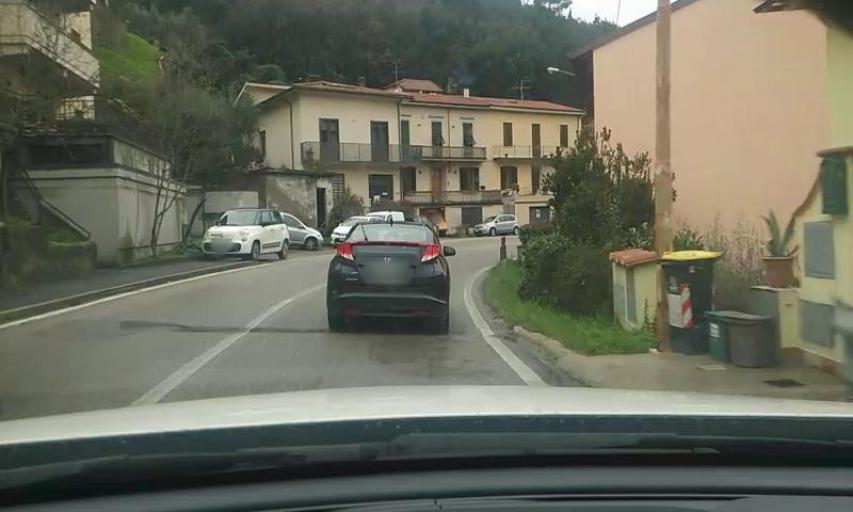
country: IT
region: Tuscany
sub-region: Provincia di Prato
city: Vaiano
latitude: 43.9349
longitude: 11.1257
